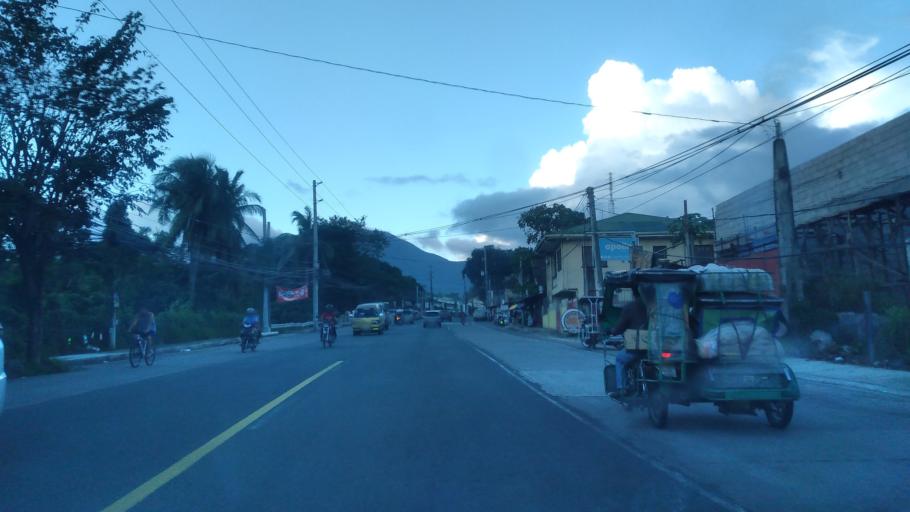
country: PH
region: Calabarzon
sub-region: Province of Quezon
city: Isabang
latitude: 13.9645
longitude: 121.5648
